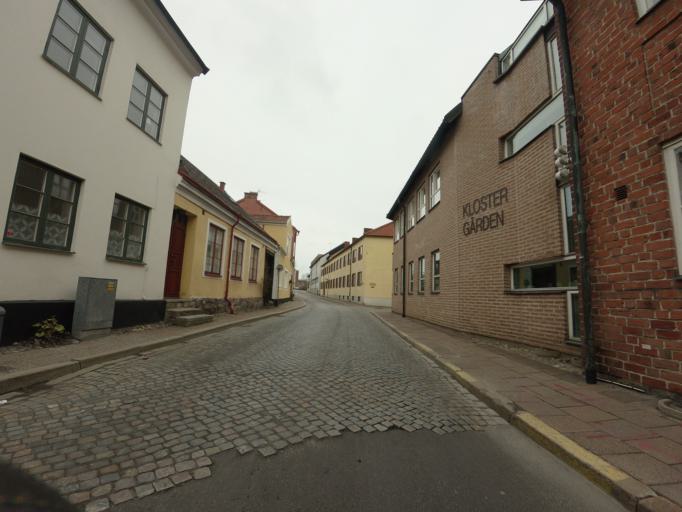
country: SE
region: Skane
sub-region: Ystads Kommun
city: Ystad
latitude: 55.4315
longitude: 13.8189
